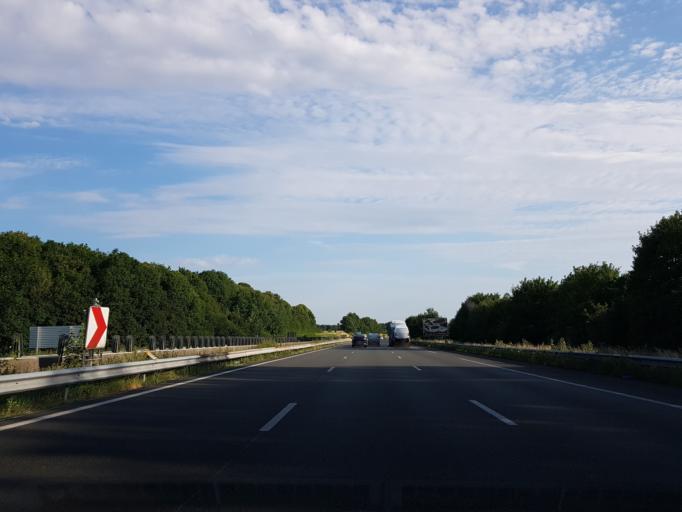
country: FR
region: Picardie
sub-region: Departement de la Somme
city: Peronne
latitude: 49.9985
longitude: 2.8751
